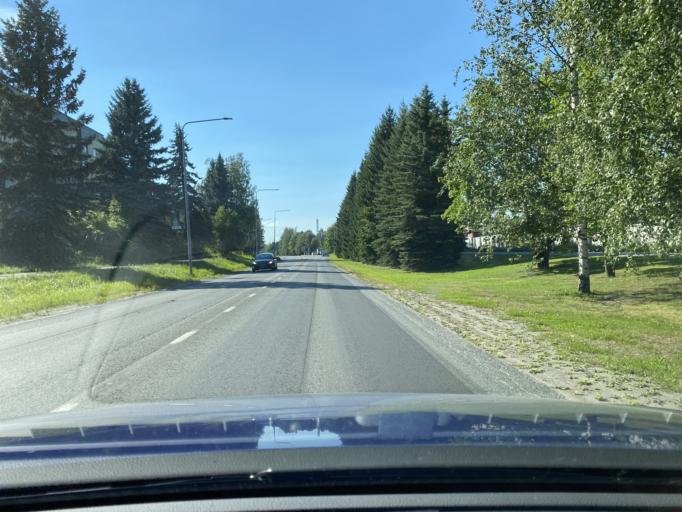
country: FI
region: Pirkanmaa
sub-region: Tampere
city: Tampere
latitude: 61.4928
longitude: 23.8413
